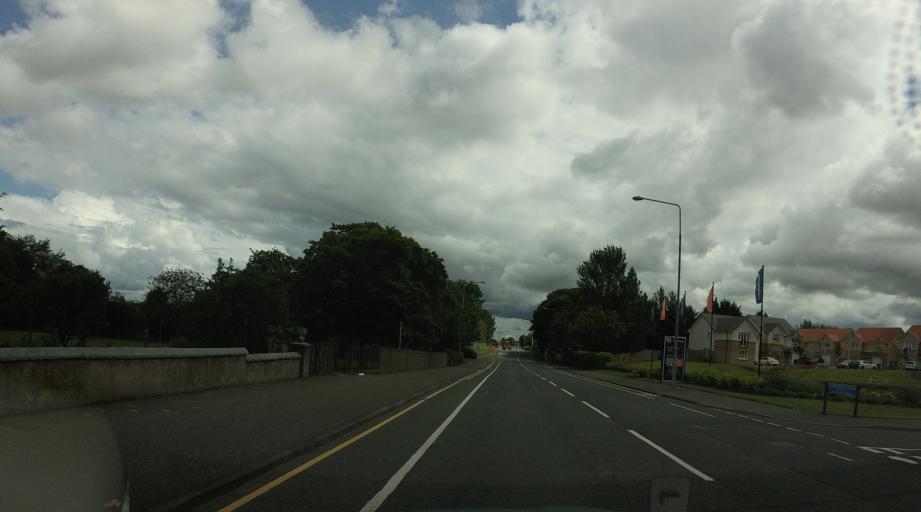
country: GB
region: Scotland
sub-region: West Lothian
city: Broxburn
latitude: 55.9344
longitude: -3.4588
